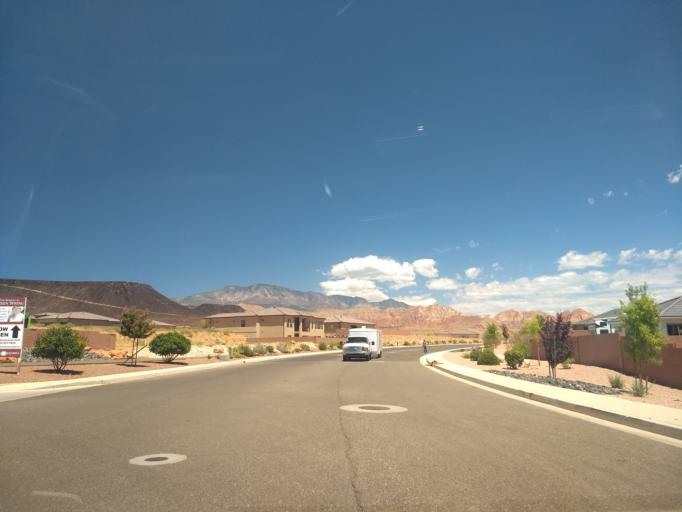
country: US
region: Utah
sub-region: Washington County
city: Washington
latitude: 37.1568
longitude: -113.5315
